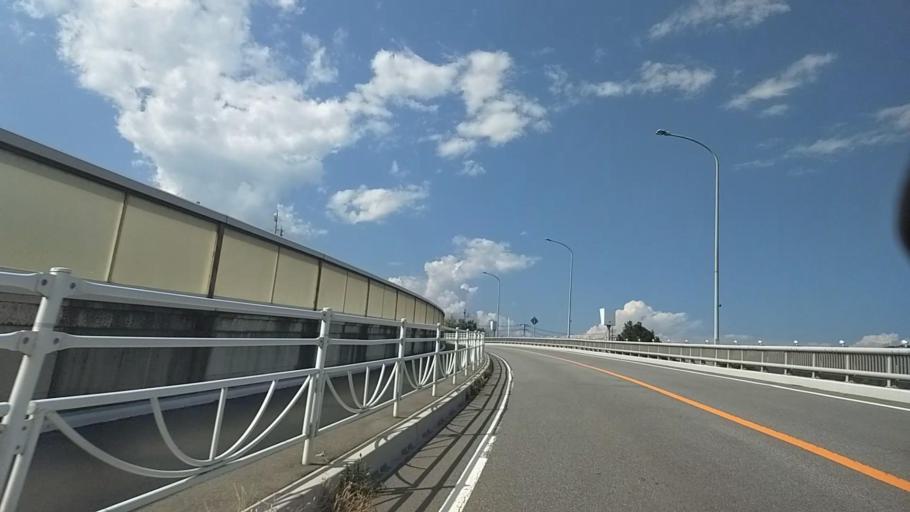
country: JP
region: Shizuoka
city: Fujinomiya
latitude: 35.3815
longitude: 138.4490
